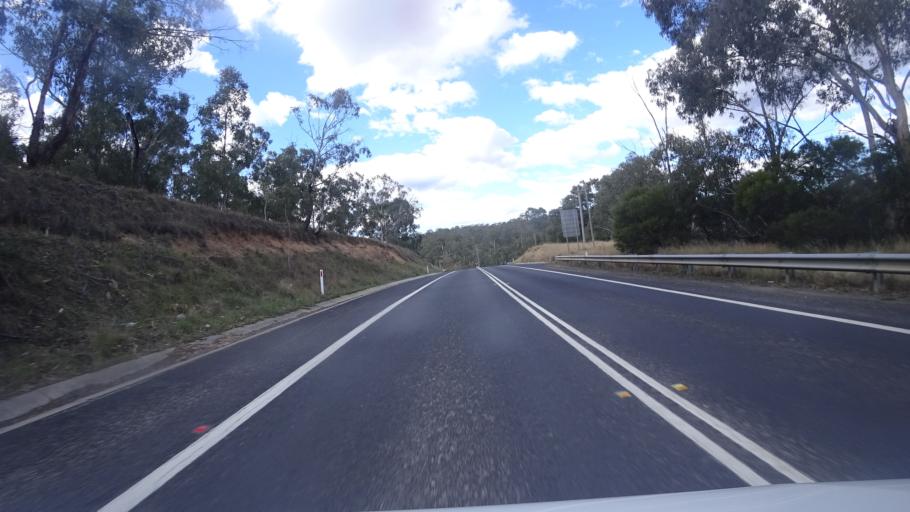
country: AU
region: New South Wales
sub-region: Lithgow
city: Bowenfels
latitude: -33.5434
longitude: 150.1658
